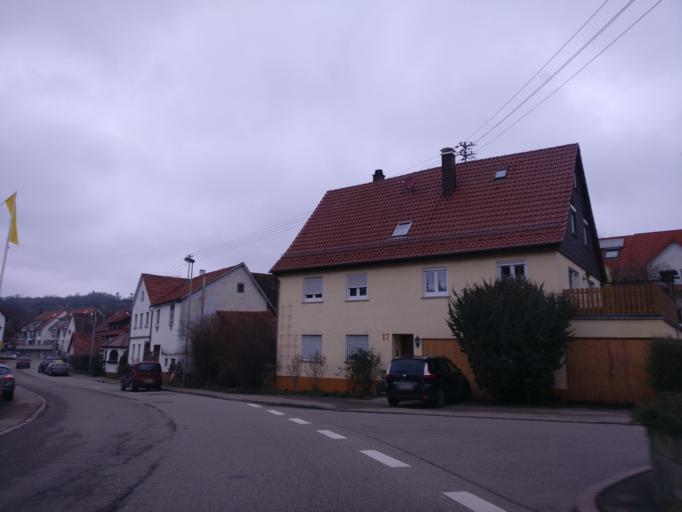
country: DE
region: Baden-Wuerttemberg
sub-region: Regierungsbezirk Stuttgart
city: Allmersbach im Tal
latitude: 48.8613
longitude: 9.4716
